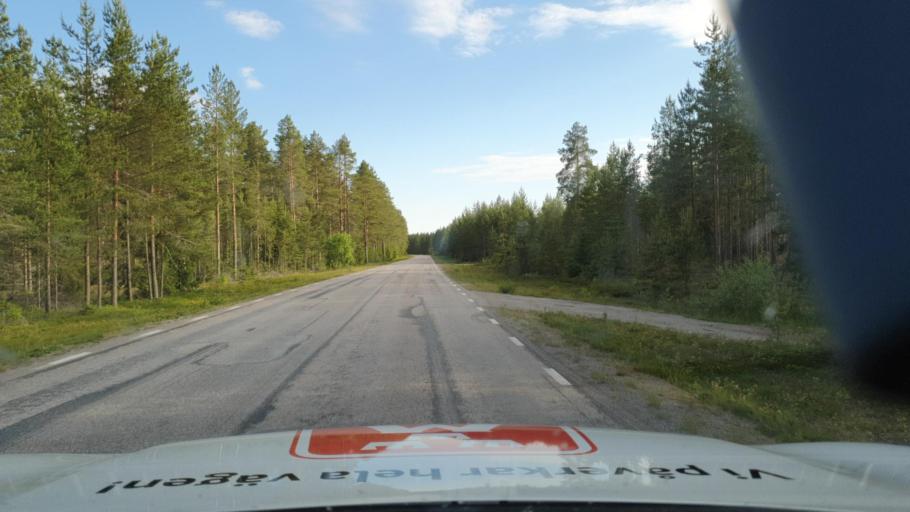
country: SE
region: Vaesterbotten
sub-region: Umea Kommun
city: Roback
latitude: 63.8711
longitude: 20.1489
